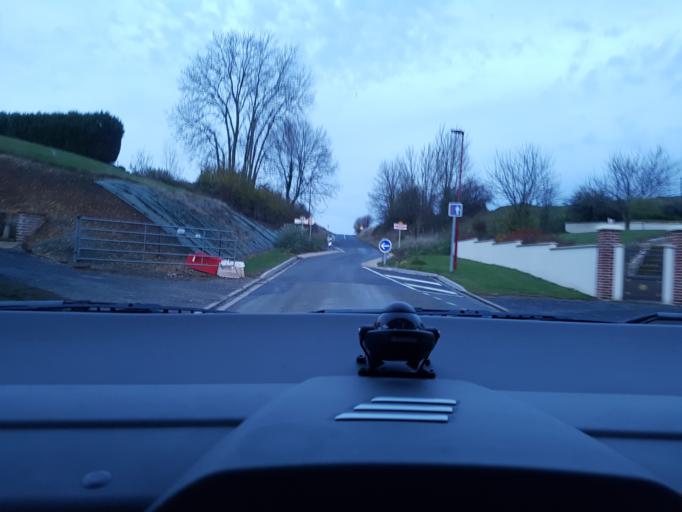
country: FR
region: Picardie
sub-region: Departement de la Somme
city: Beauquesne
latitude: 50.0583
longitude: 2.4139
